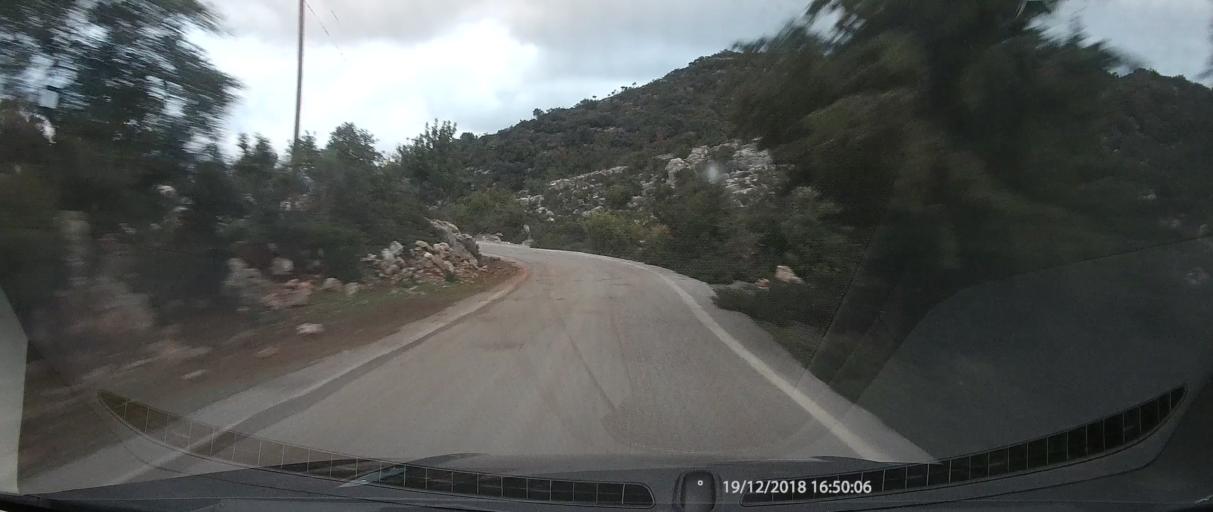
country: GR
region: Peloponnese
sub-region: Nomos Lakonias
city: Sykea
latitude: 36.9504
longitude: 22.9961
